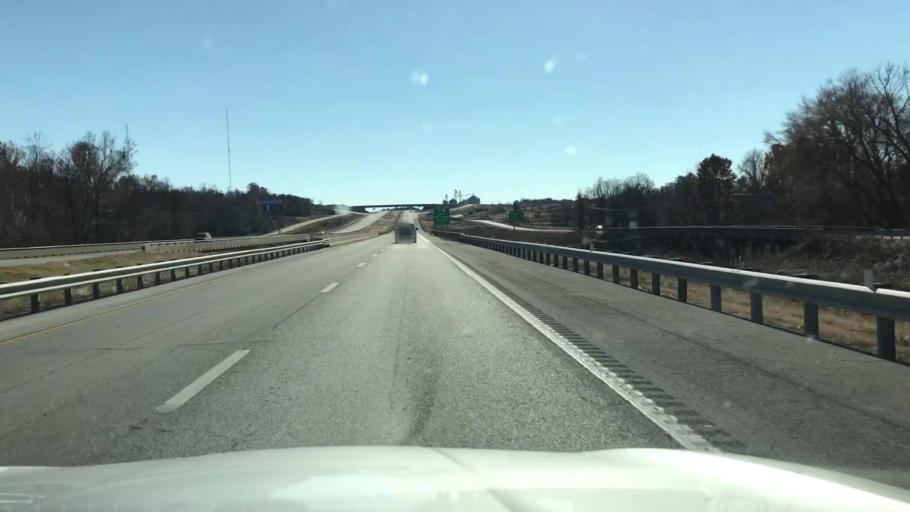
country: US
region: Missouri
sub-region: Jasper County
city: Carthage
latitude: 37.1064
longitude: -94.3103
